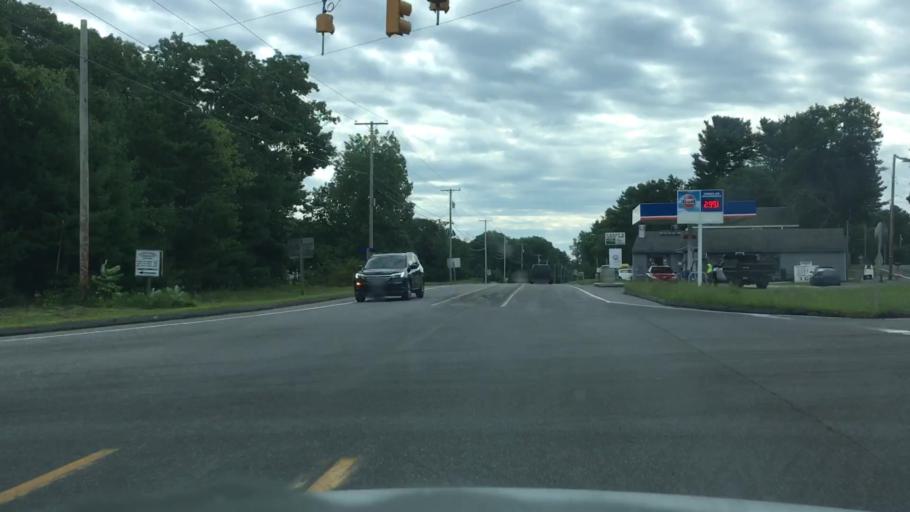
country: US
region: Maine
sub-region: York County
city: Wells Beach Station
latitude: 43.3323
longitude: -70.6260
